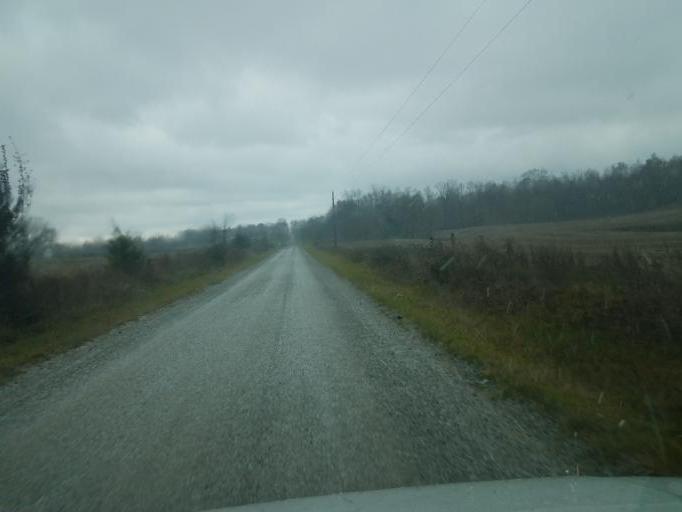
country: US
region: Ohio
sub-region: Morrow County
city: Mount Gilead
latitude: 40.5407
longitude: -82.7108
